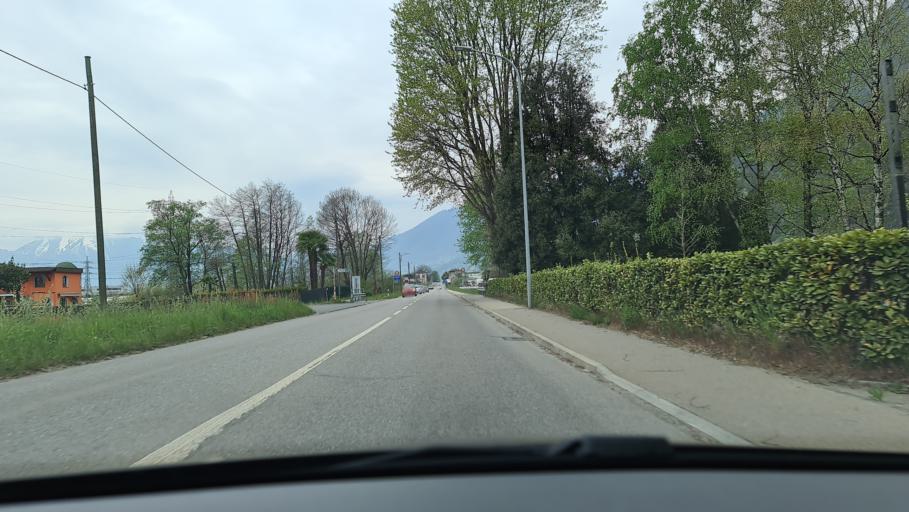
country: CH
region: Ticino
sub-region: Locarno District
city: Cugnasco
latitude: 46.1736
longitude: 8.9056
